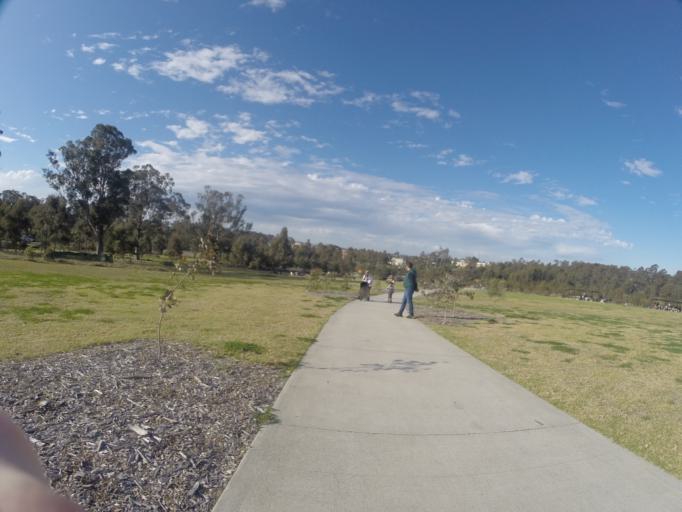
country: AU
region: New South Wales
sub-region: Fairfield
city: Horsley Park
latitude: -33.8517
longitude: 150.8731
